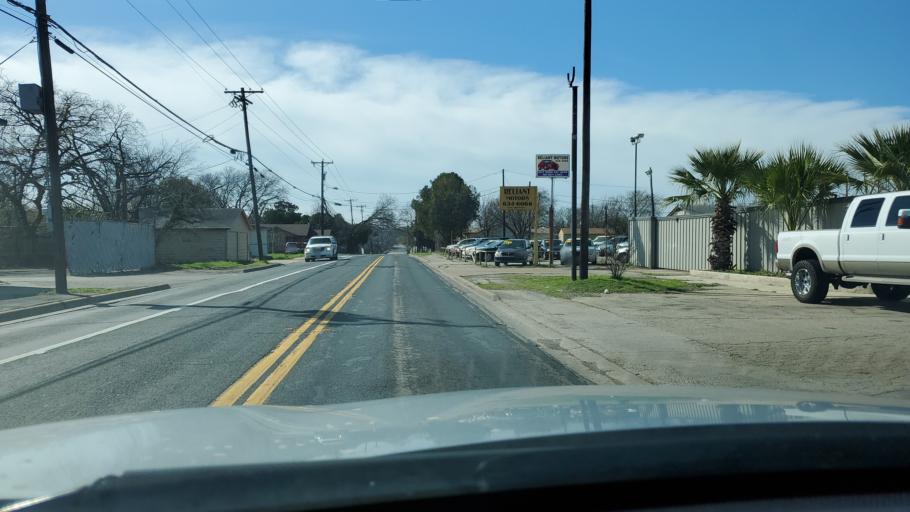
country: US
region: Texas
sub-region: Bell County
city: Killeen
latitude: 31.1164
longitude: -97.7267
